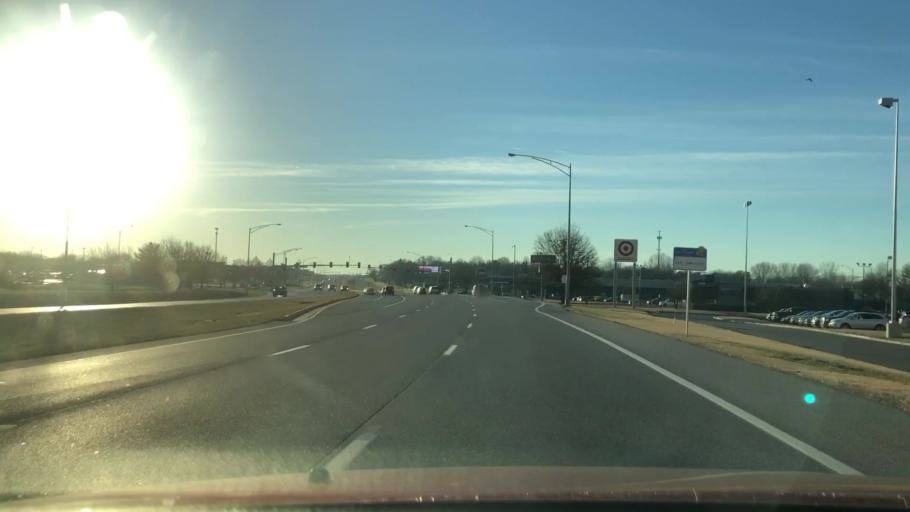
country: US
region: Missouri
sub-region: Greene County
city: Springfield
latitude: 37.1522
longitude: -93.2620
